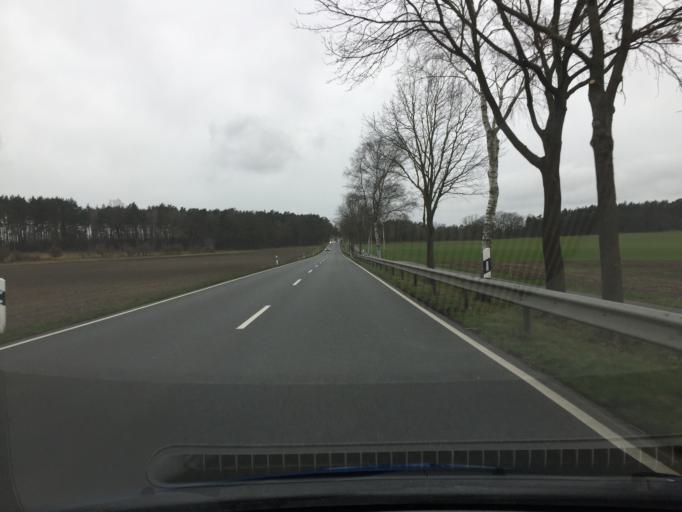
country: DE
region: Lower Saxony
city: Stoetze
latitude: 53.0315
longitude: 10.7764
